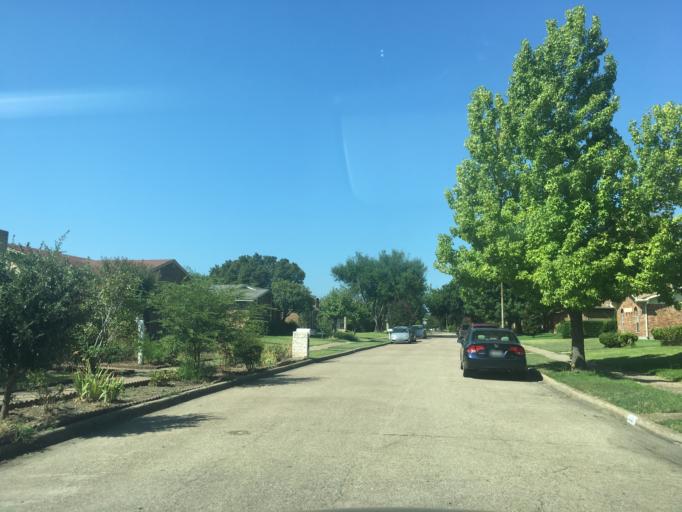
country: US
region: Texas
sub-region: Dallas County
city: Garland
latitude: 32.8545
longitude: -96.6578
